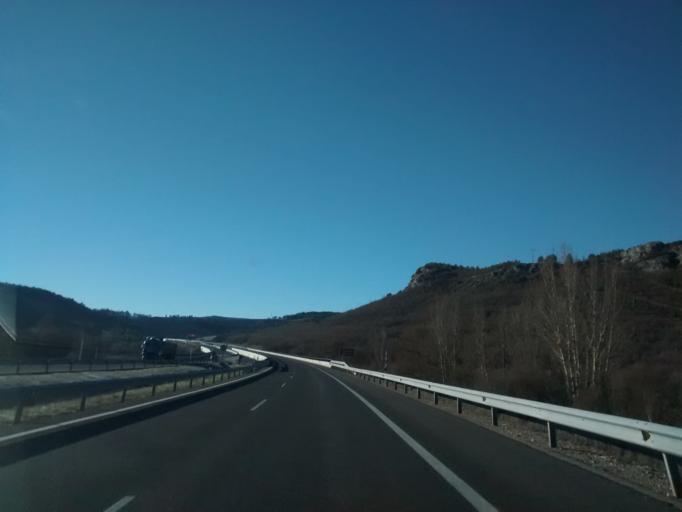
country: ES
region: Castille and Leon
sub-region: Provincia de Palencia
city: Alar del Rey
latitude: 42.6969
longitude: -4.2971
